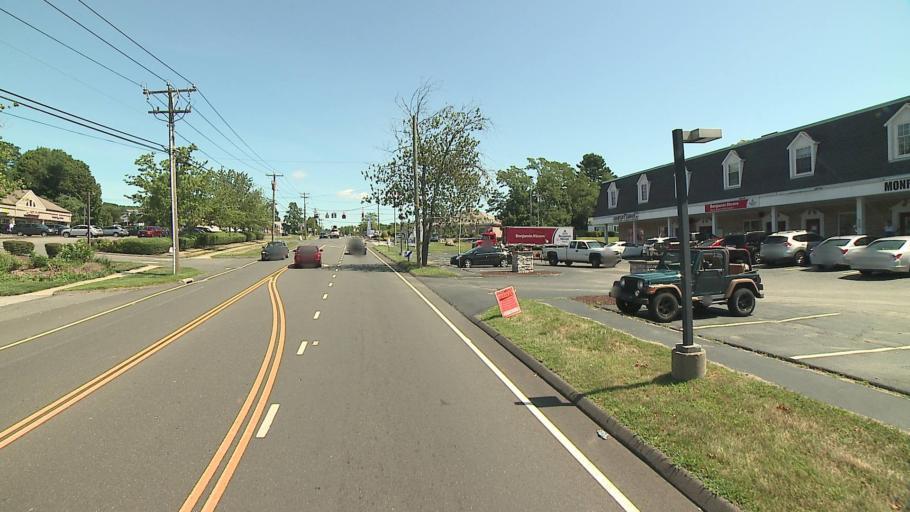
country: US
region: Connecticut
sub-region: Fairfield County
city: Trumbull
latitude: 41.3135
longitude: -73.2192
